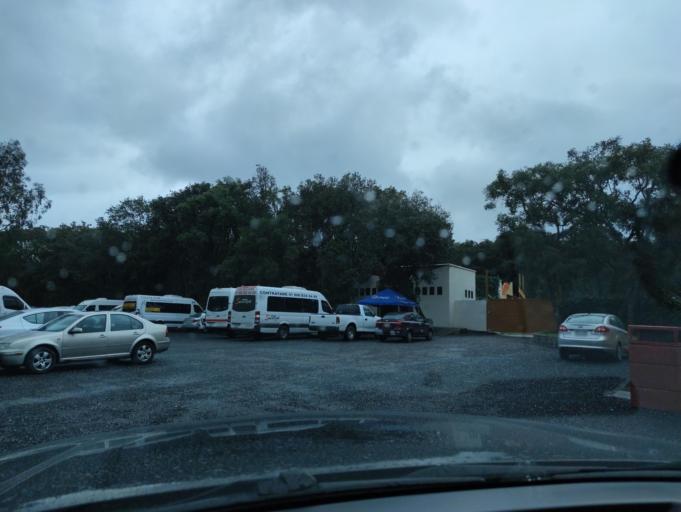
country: MX
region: Mexico
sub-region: Morelos
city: San Marcos Tlazalpan
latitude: 19.8719
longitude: -99.6607
